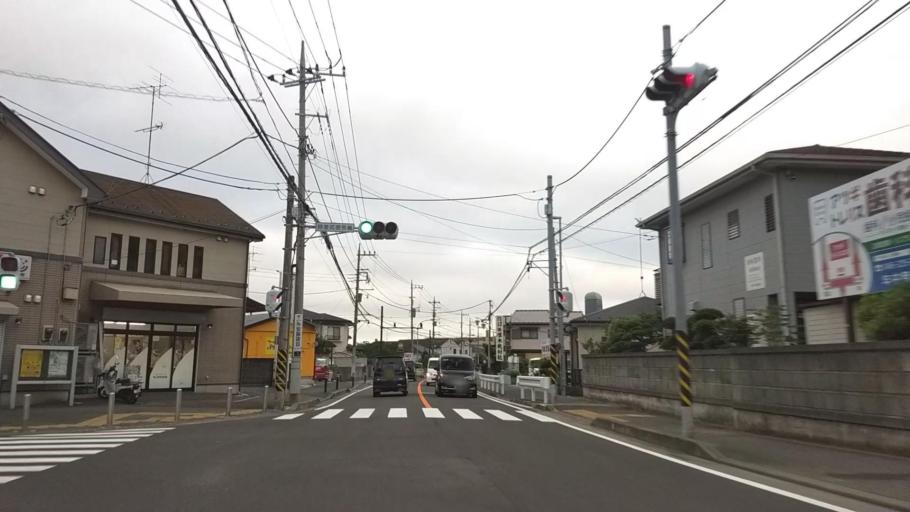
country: JP
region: Kanagawa
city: Atsugi
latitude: 35.4546
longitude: 139.3497
